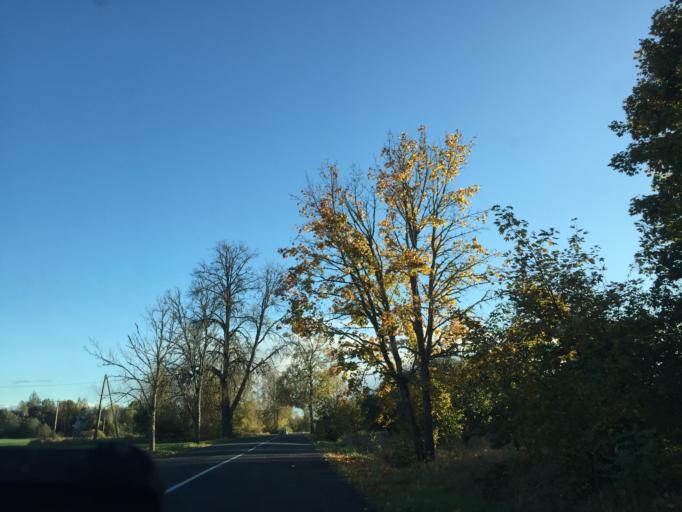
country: LV
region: Broceni
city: Broceni
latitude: 56.8518
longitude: 22.3868
